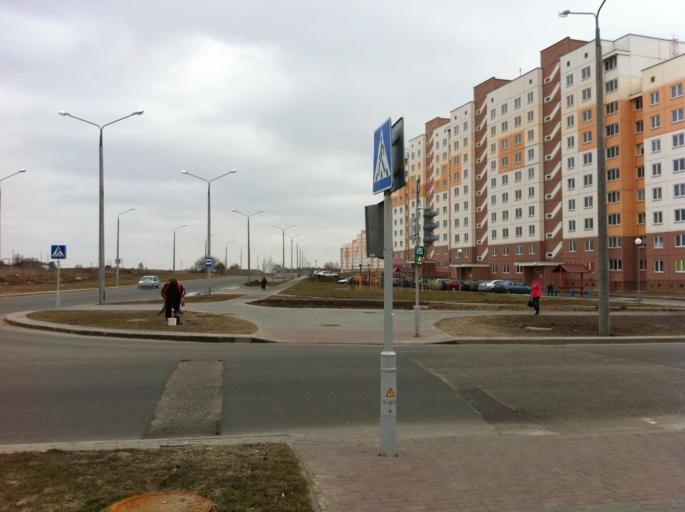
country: BY
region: Grodnenskaya
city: Hrodna
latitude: 53.7147
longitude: 23.8585
